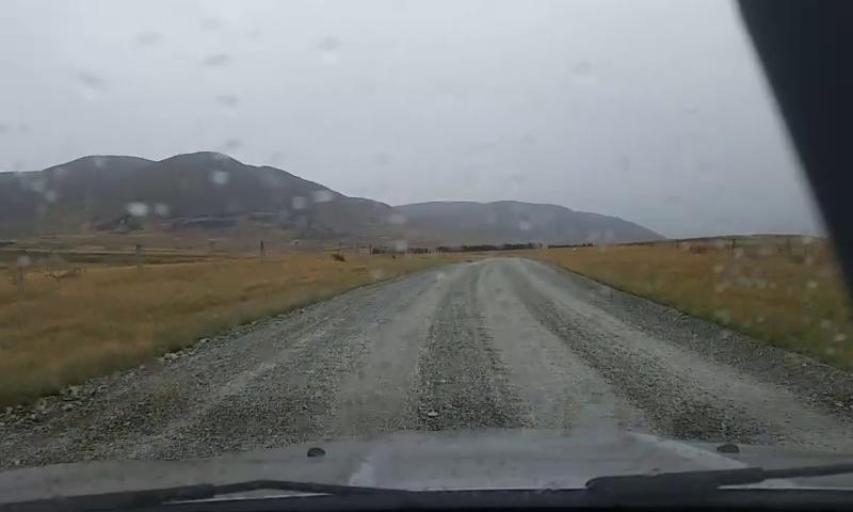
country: NZ
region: Canterbury
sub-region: Ashburton District
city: Methven
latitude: -43.6167
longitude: 171.0842
